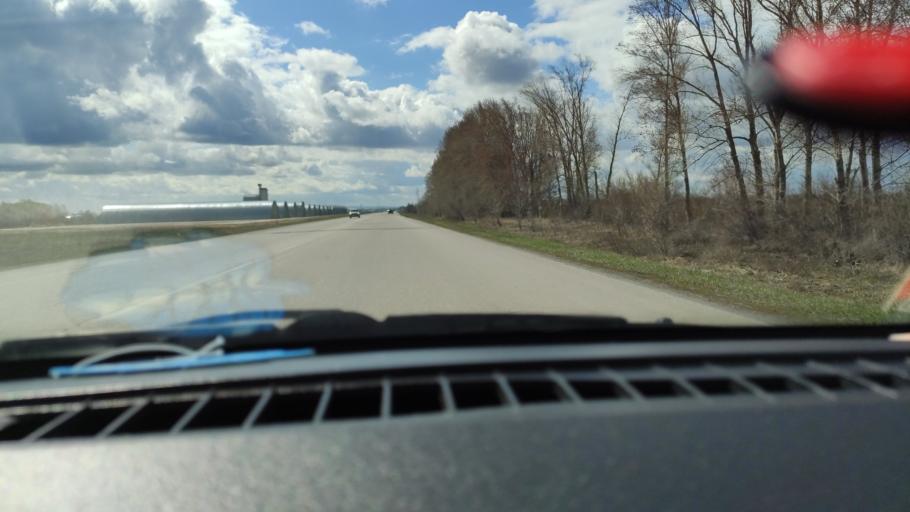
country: RU
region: Samara
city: Tol'yatti
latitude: 53.6880
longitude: 49.4176
